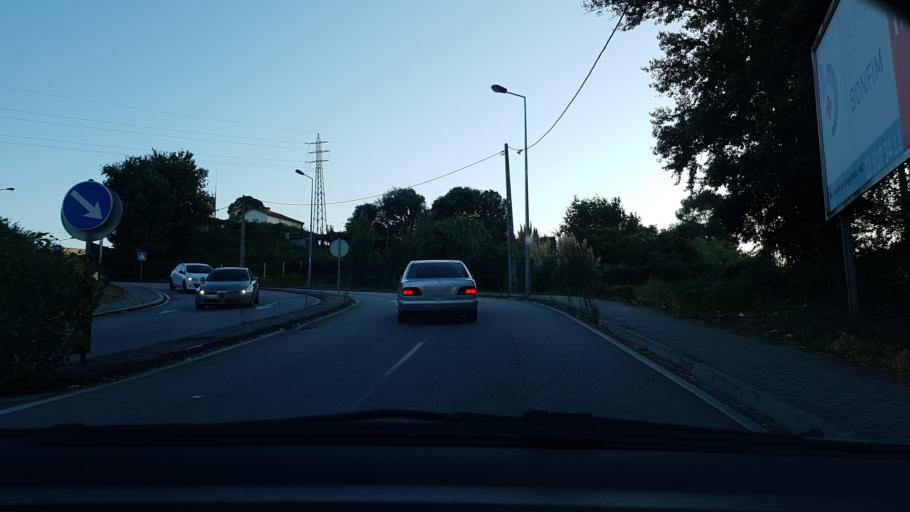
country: PT
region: Porto
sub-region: Gondomar
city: Rio Tinto
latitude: 41.1774
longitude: -8.5644
